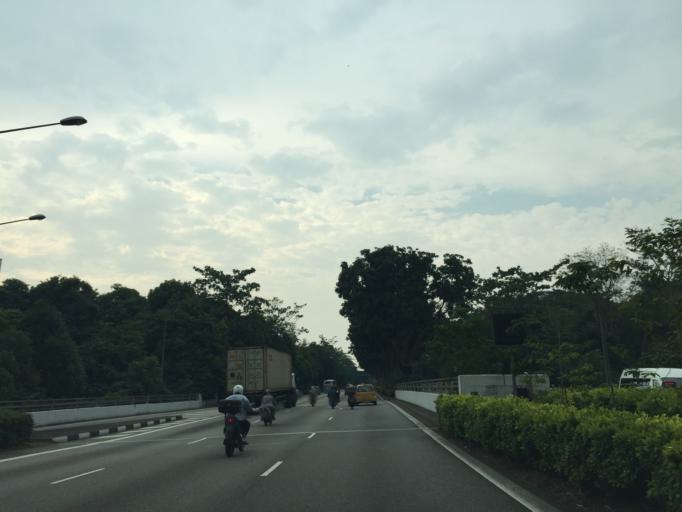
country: MY
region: Johor
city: Johor Bahru
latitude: 1.3767
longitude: 103.7768
